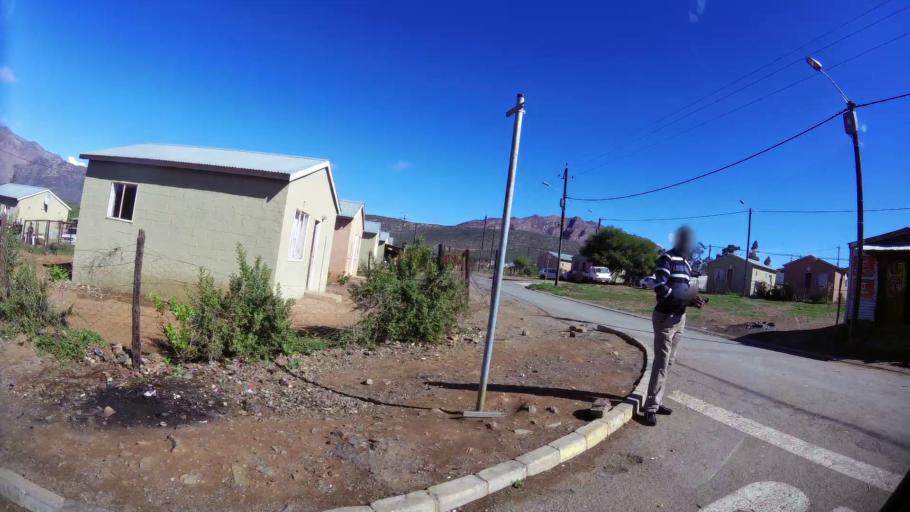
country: ZA
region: Western Cape
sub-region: Cape Winelands District Municipality
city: Ashton
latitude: -33.7711
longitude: 20.1411
